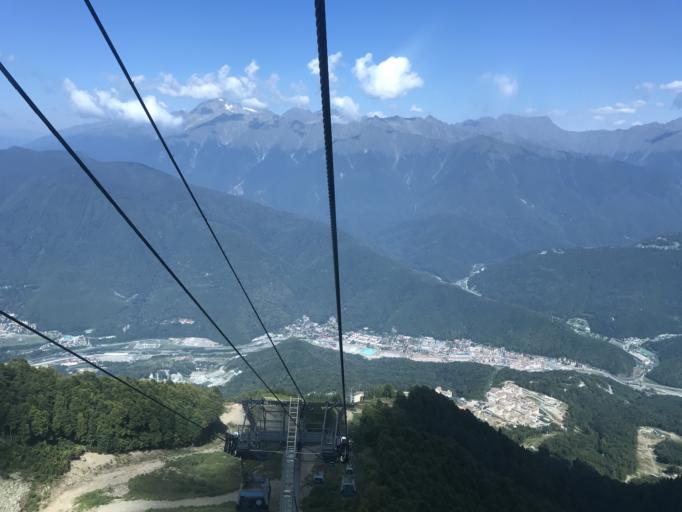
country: RU
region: Krasnodarskiy
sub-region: Sochi City
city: Krasnaya Polyana
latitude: 43.6486
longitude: 40.2510
